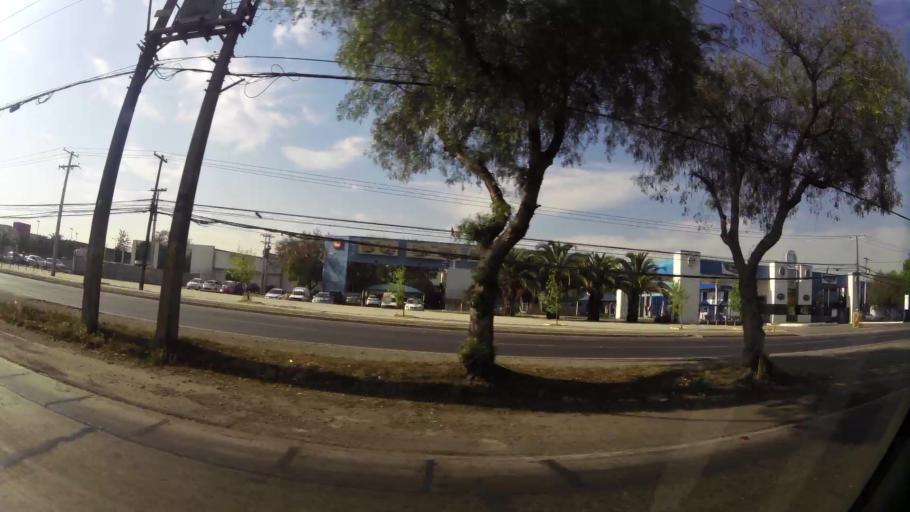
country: CL
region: Santiago Metropolitan
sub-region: Provincia de Santiago
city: Lo Prado
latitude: -33.5126
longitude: -70.7289
